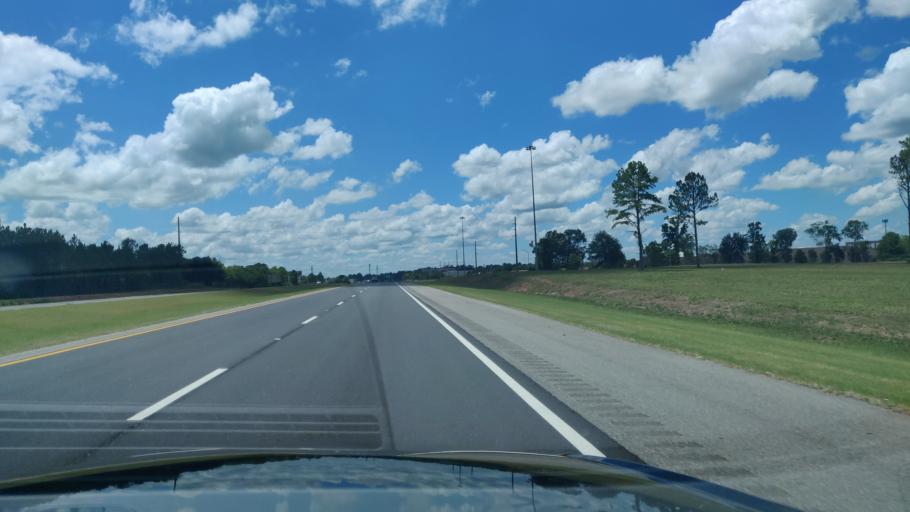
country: US
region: Georgia
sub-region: Dougherty County
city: Albany
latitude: 31.6177
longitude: -84.2049
